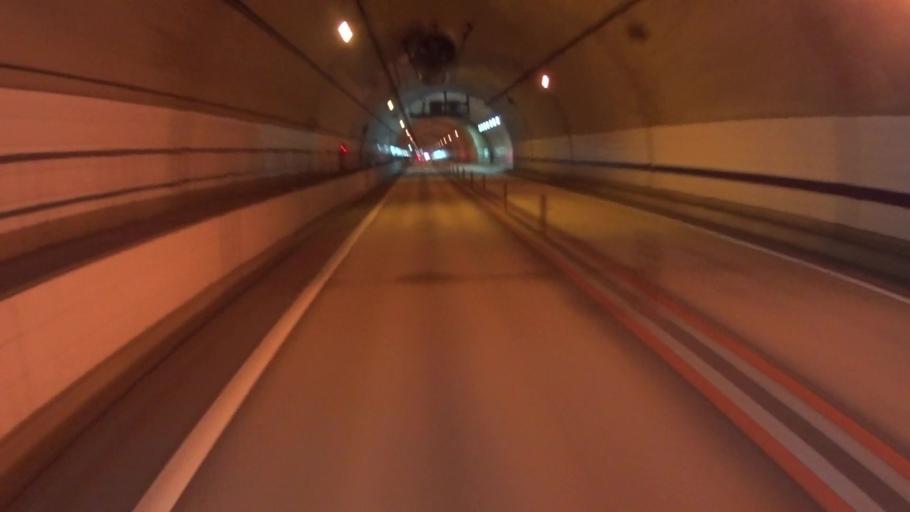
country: JP
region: Kyoto
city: Miyazu
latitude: 35.4862
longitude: 135.1726
